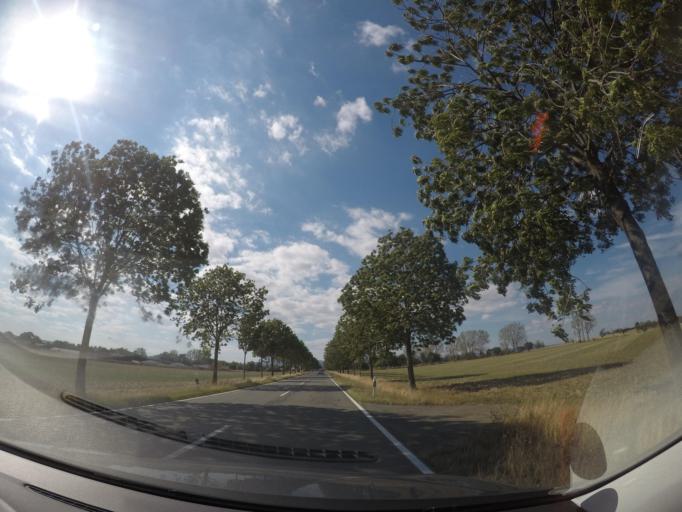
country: DE
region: Saxony-Anhalt
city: Langeln
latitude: 51.9190
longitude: 10.7953
